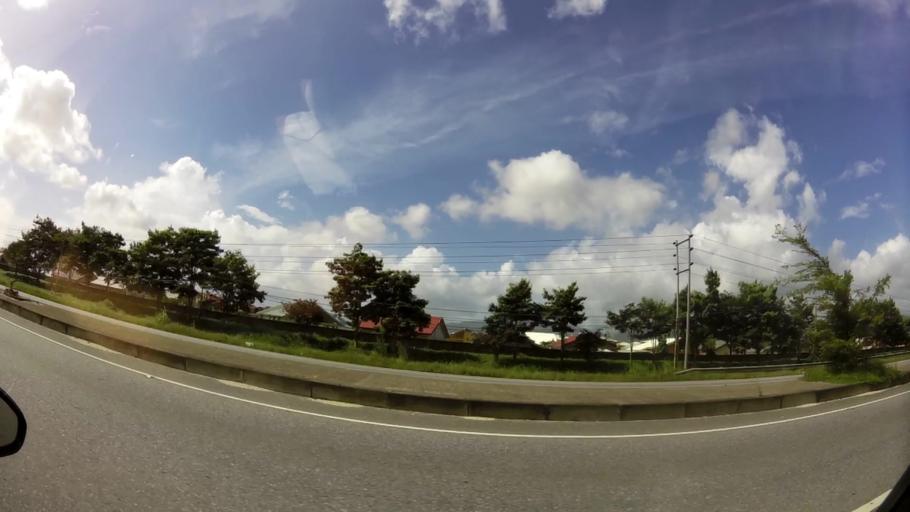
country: TT
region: Borough of Arima
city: Arima
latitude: 10.6104
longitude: -61.2659
